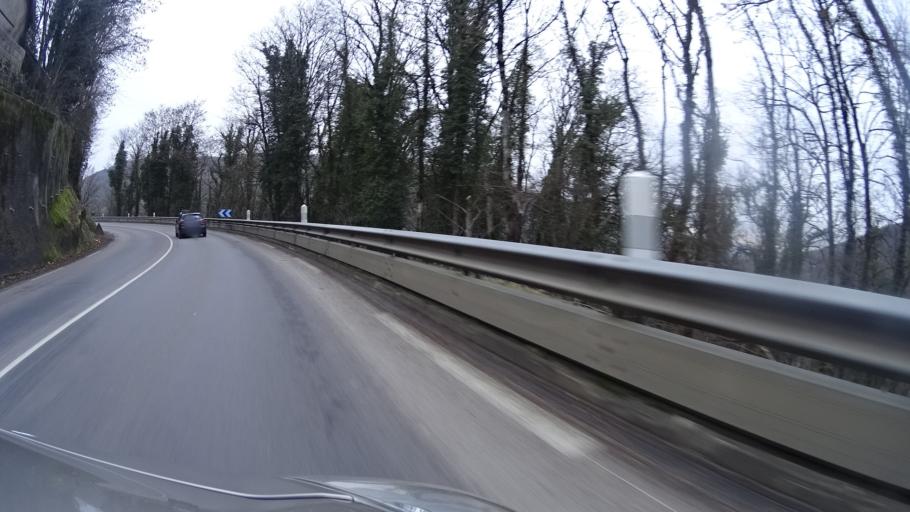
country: FR
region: Franche-Comte
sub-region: Departement du Doubs
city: Morre
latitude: 47.2300
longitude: 6.0619
